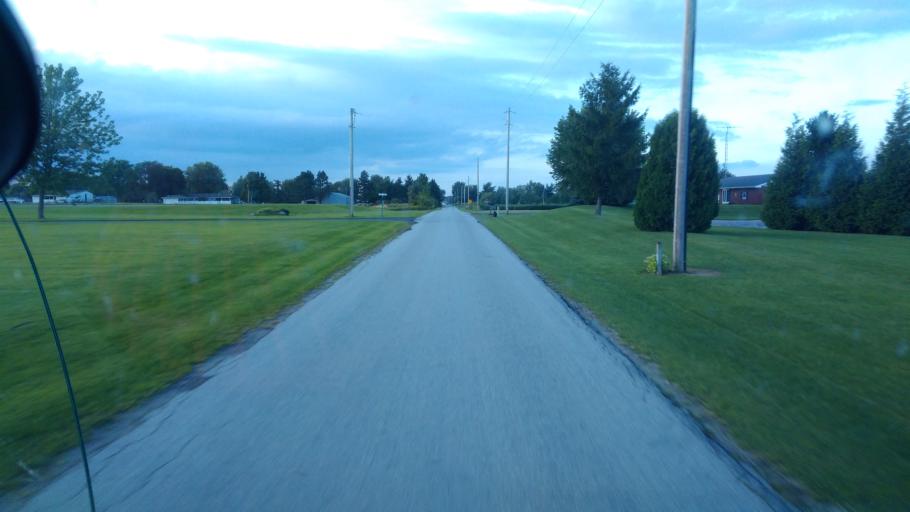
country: US
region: Ohio
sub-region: Hardin County
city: Kenton
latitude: 40.6398
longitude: -83.5153
